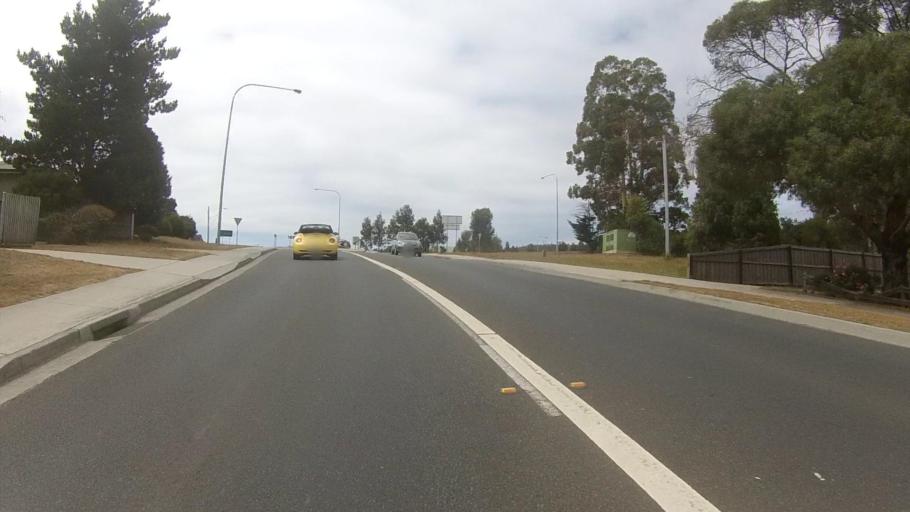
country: AU
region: Tasmania
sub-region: Kingborough
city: Kingston
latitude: -42.9745
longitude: 147.3000
